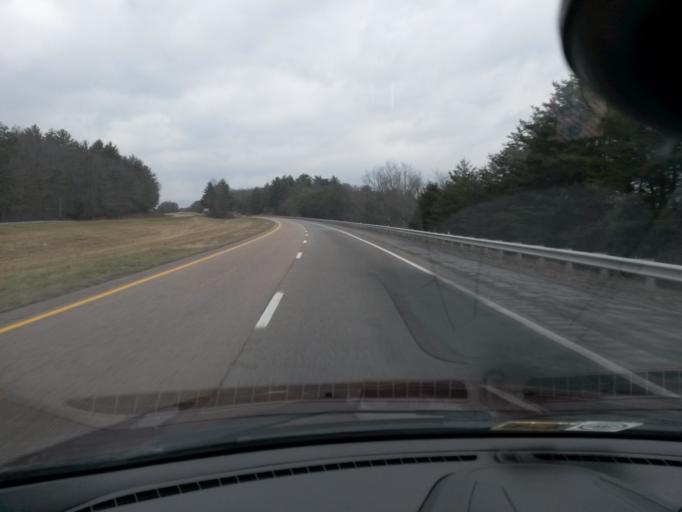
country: US
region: Virginia
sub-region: Alleghany County
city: Clifton Forge
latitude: 37.8189
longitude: -79.7418
